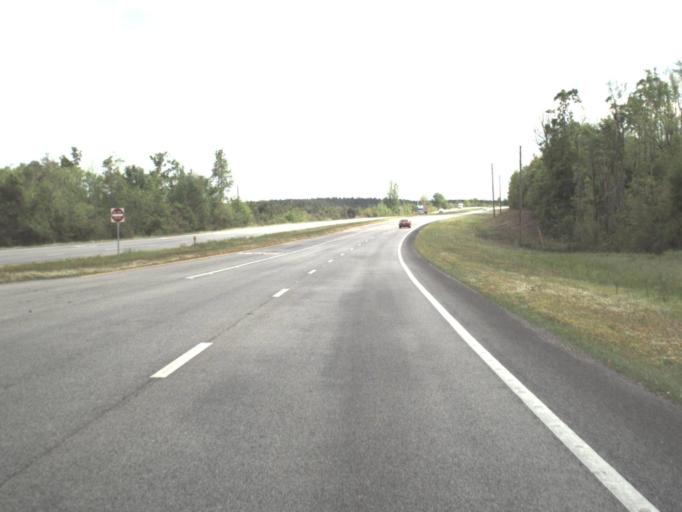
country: US
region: Florida
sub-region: Escambia County
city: Molino
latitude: 30.7964
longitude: -87.3344
